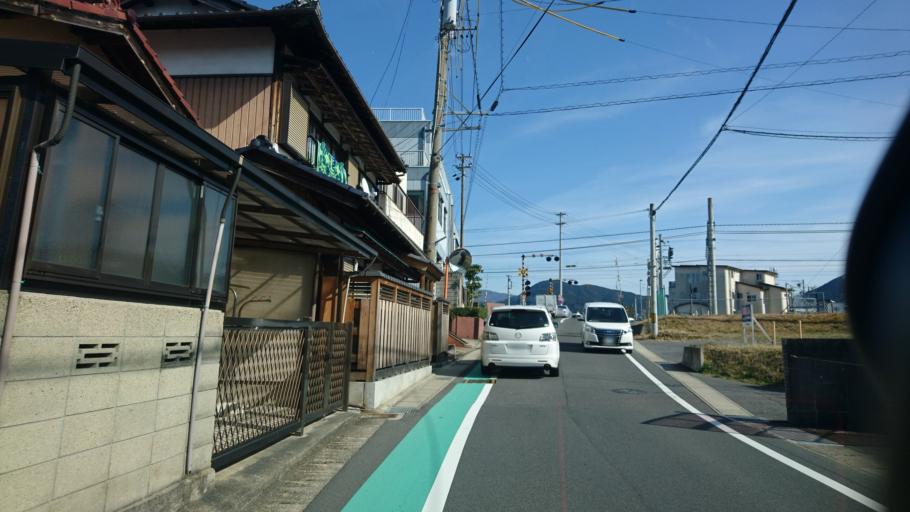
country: JP
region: Gifu
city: Nakatsugawa
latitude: 35.4564
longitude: 137.4089
